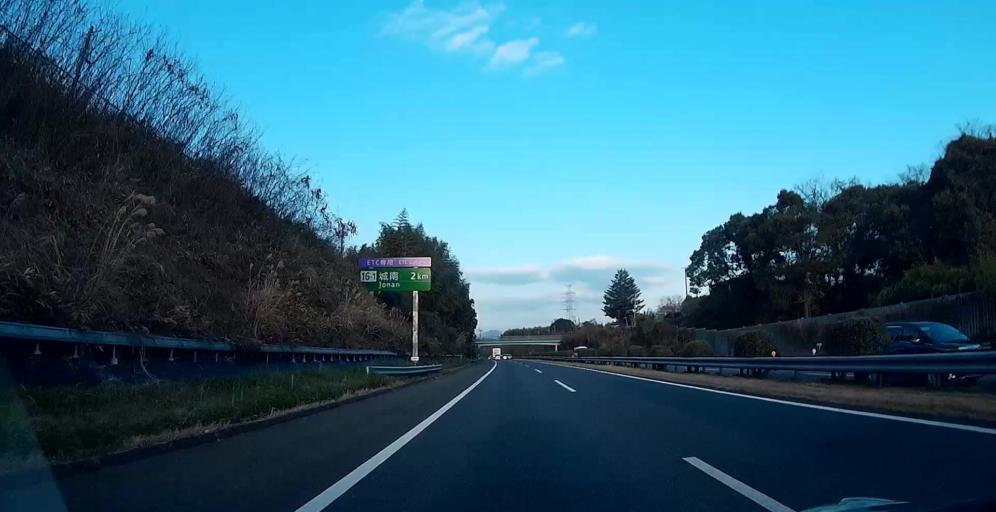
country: JP
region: Kumamoto
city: Uto
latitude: 32.6788
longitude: 130.7273
